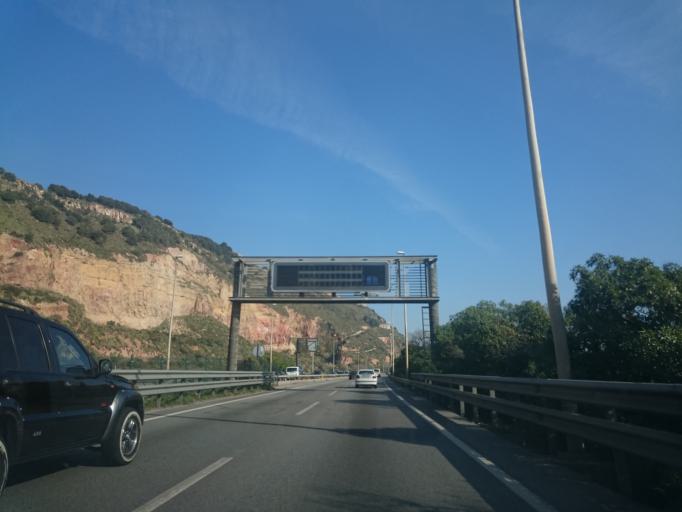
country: ES
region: Catalonia
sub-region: Provincia de Barcelona
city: Sants-Montjuic
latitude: 41.3547
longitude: 2.1597
